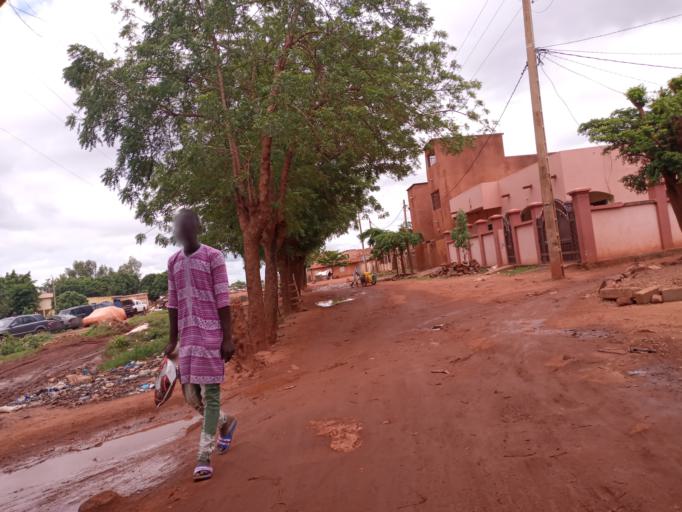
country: ML
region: Bamako
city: Bamako
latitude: 12.5476
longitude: -7.9969
